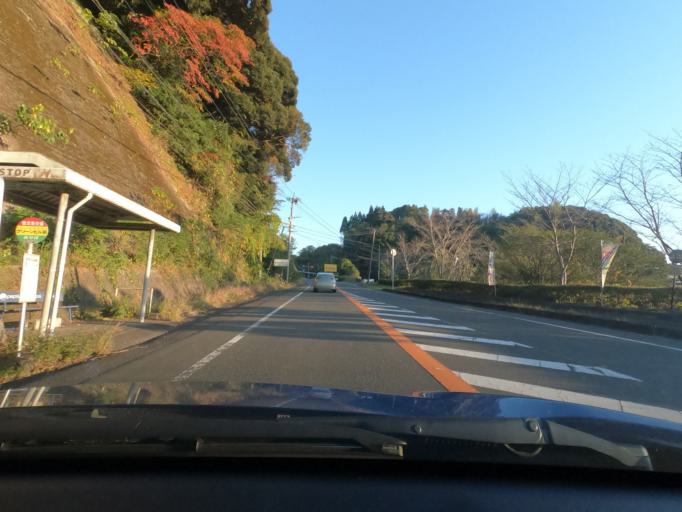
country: JP
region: Kagoshima
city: Satsumasendai
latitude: 31.7972
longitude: 130.4199
